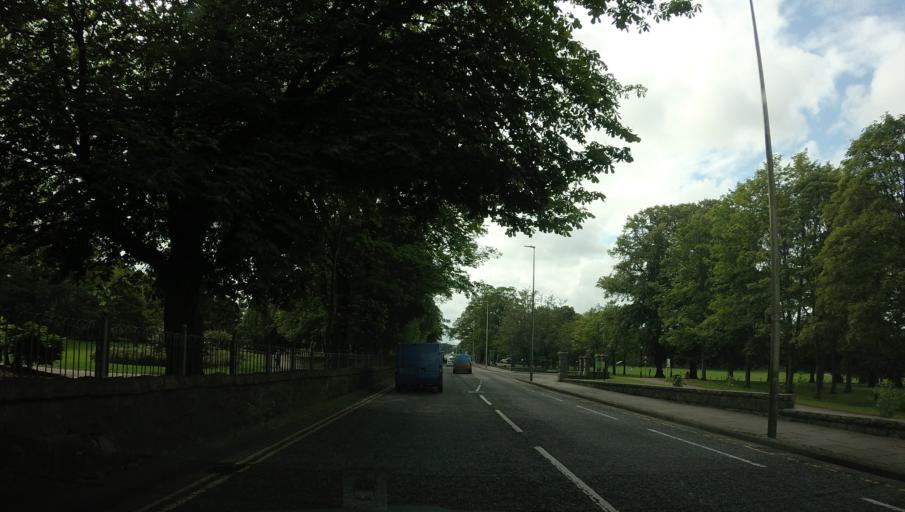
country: GB
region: Scotland
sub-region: Aberdeen City
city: Aberdeen
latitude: 57.1527
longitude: -2.1222
